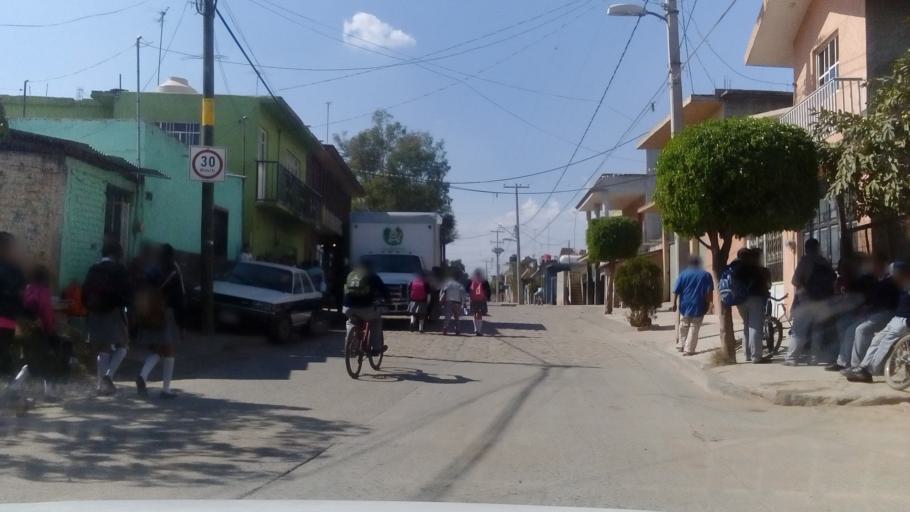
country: MX
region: Guanajuato
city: Duarte
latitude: 21.0859
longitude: -101.5206
